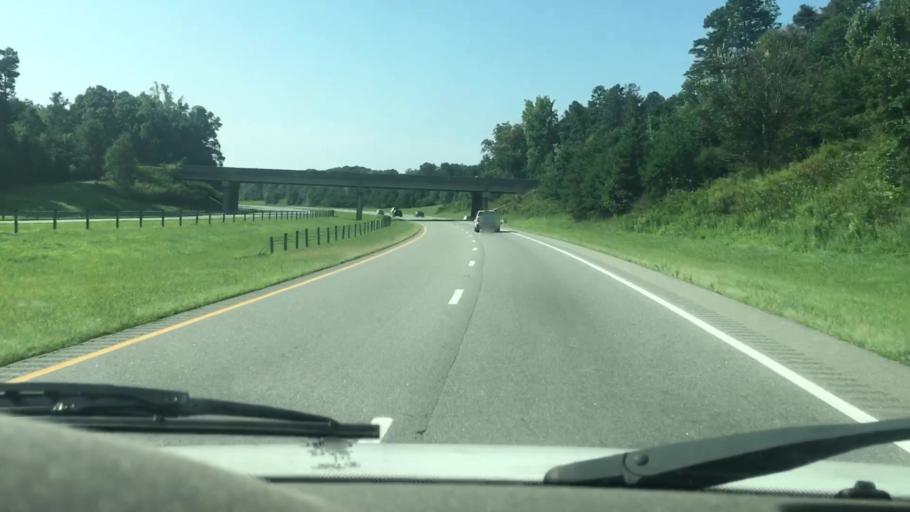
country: US
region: North Carolina
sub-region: Lincoln County
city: Lowesville
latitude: 35.3840
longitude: -81.0011
